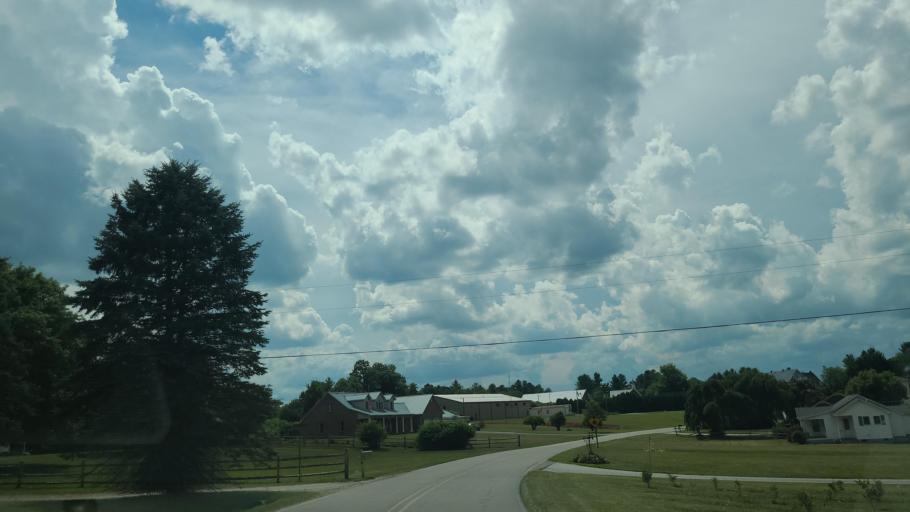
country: US
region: North Carolina
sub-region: Ashe County
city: Jefferson
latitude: 36.3441
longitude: -81.3782
